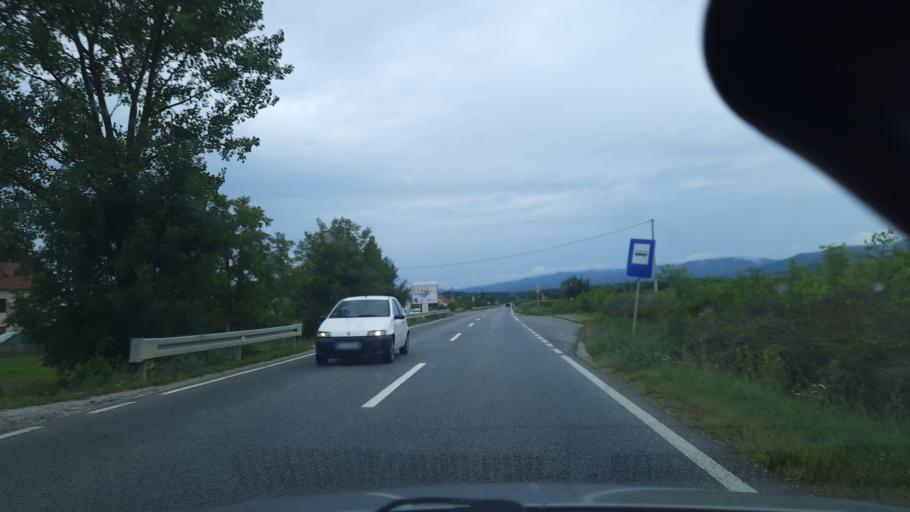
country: RS
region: Central Serbia
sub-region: Sumadijski Okrug
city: Knic
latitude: 43.9239
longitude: 20.7731
